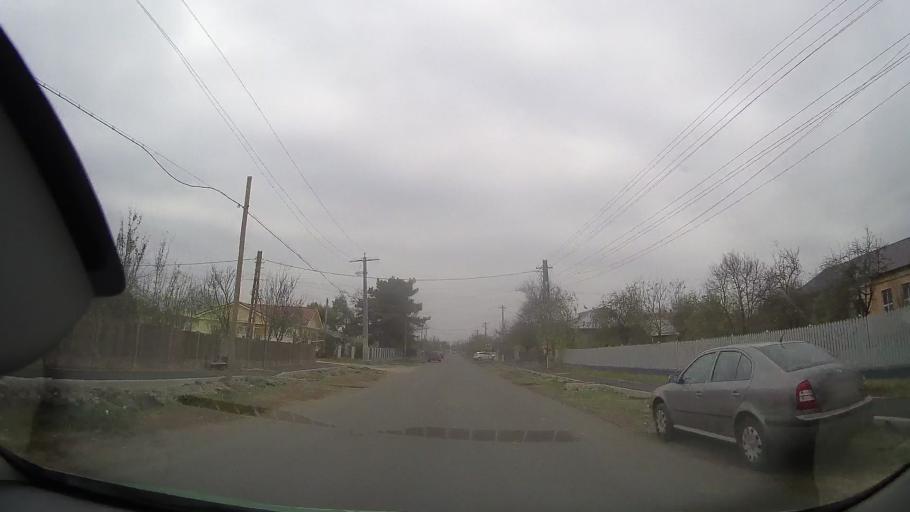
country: RO
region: Buzau
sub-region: Comuna Pogoanele
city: Pogoanele
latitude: 44.9232
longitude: 26.9943
